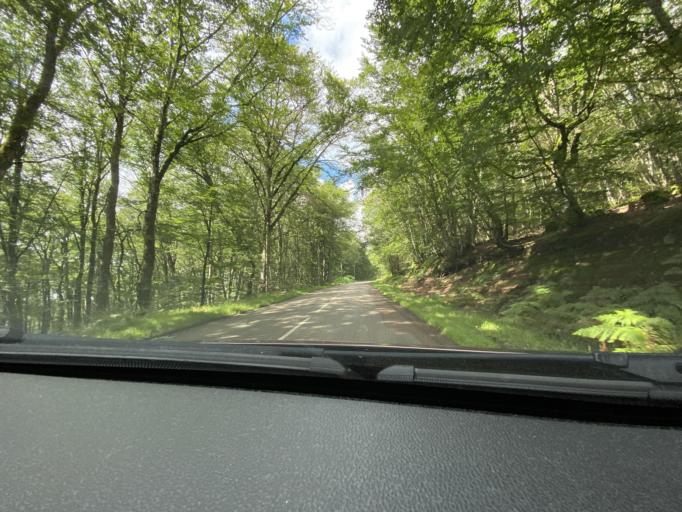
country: FR
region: Bourgogne
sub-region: Departement de la Cote-d'Or
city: Saulieu
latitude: 47.2510
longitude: 4.0719
